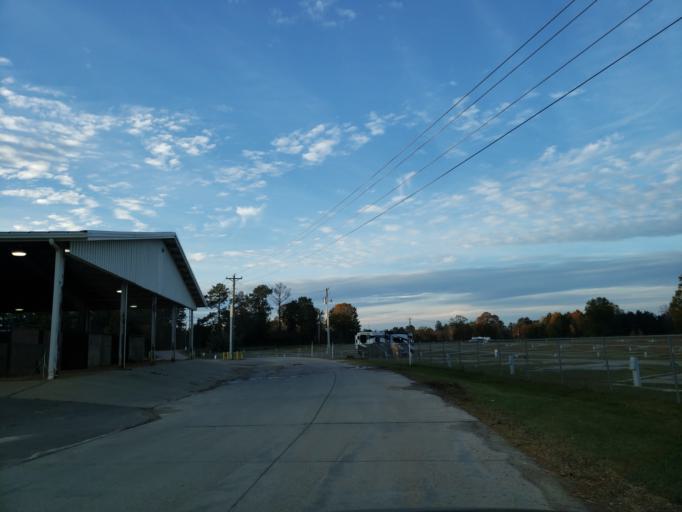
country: US
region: Mississippi
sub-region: Forrest County
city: Hattiesburg
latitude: 31.2584
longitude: -89.2742
